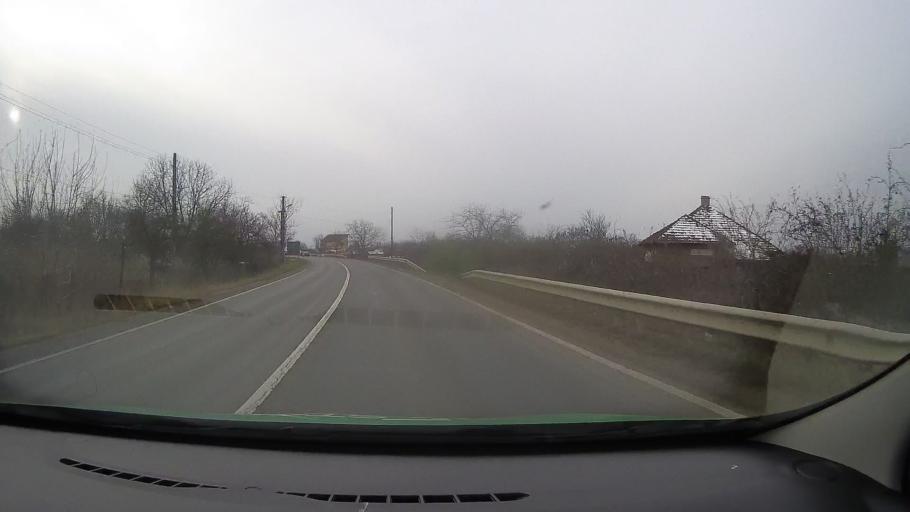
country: RO
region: Hunedoara
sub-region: Comuna Rapoltu Mare
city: Rapoltu Mare
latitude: 45.8370
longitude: 23.0539
